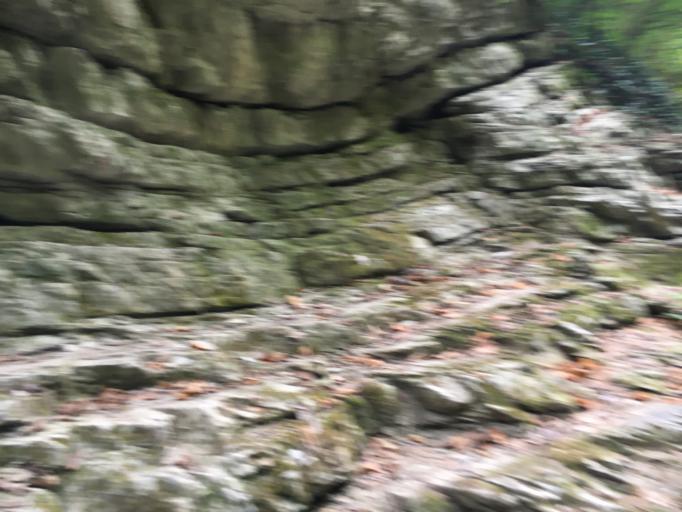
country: RU
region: Krasnodarskiy
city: Tuapse
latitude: 44.2631
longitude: 39.2082
